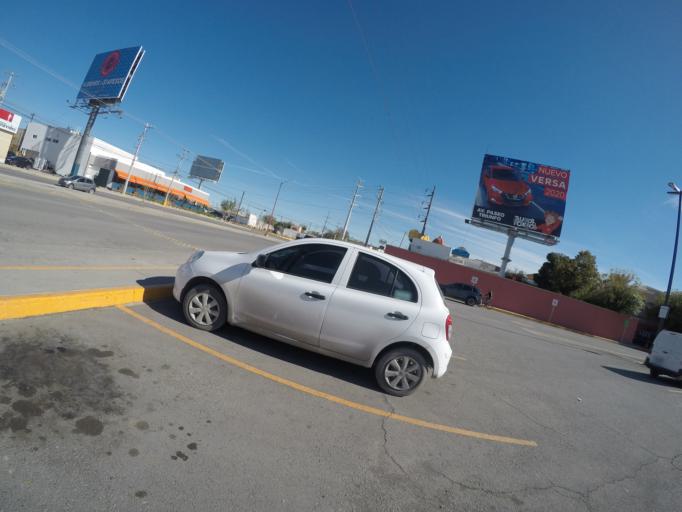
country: MX
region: Chihuahua
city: Ciudad Juarez
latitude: 31.7324
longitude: -106.4134
